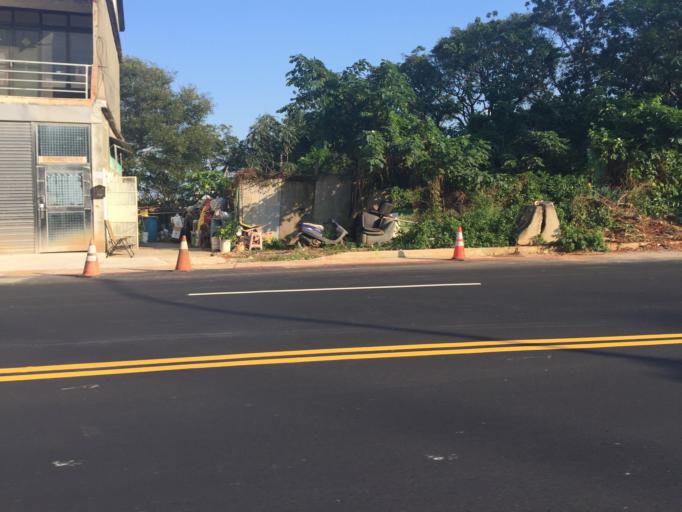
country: TW
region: Taiwan
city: Daxi
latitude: 24.9376
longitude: 121.2632
